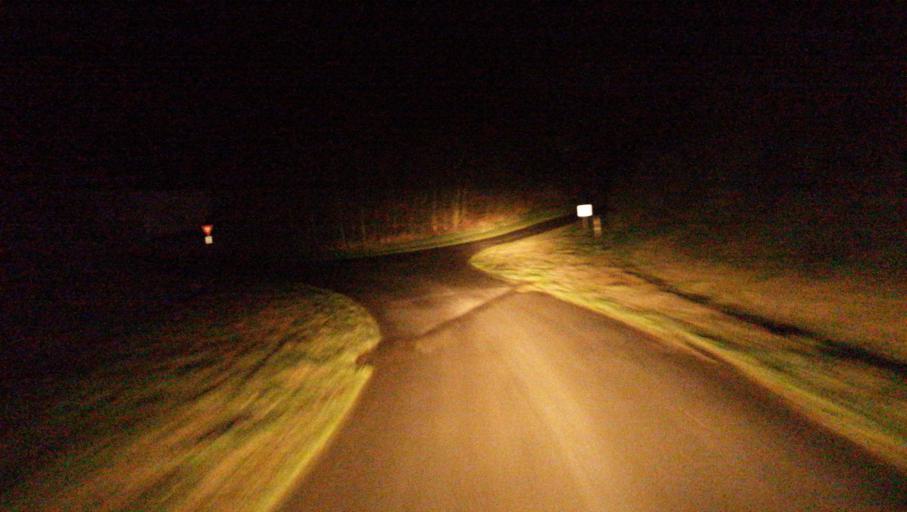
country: FR
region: Brittany
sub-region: Departement des Cotes-d'Armor
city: Plehedel
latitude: 48.6705
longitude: -3.0221
